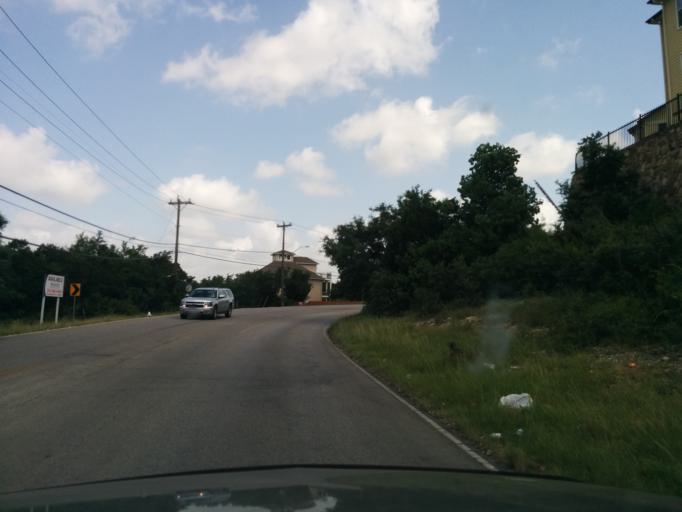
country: US
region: Texas
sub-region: Bexar County
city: Cross Mountain
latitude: 29.5955
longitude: -98.6301
